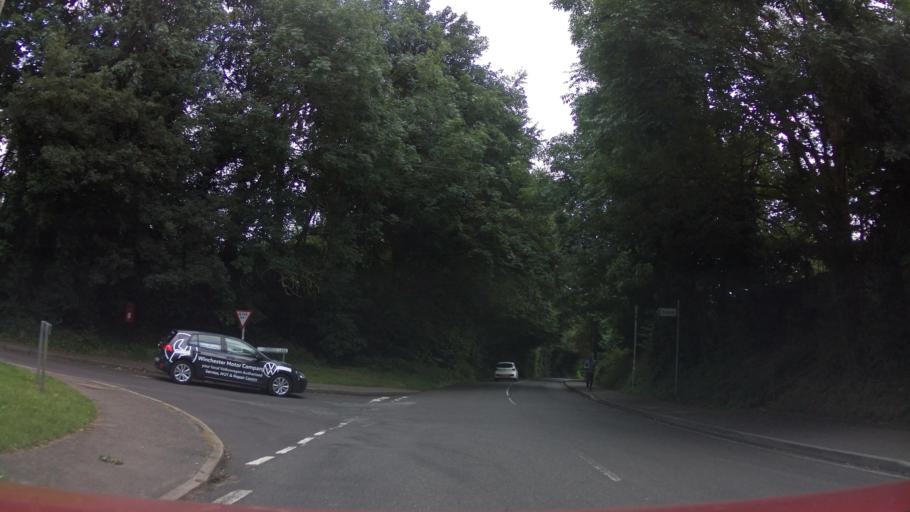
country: GB
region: England
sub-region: Hampshire
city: Overton
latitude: 51.2352
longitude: -1.3361
